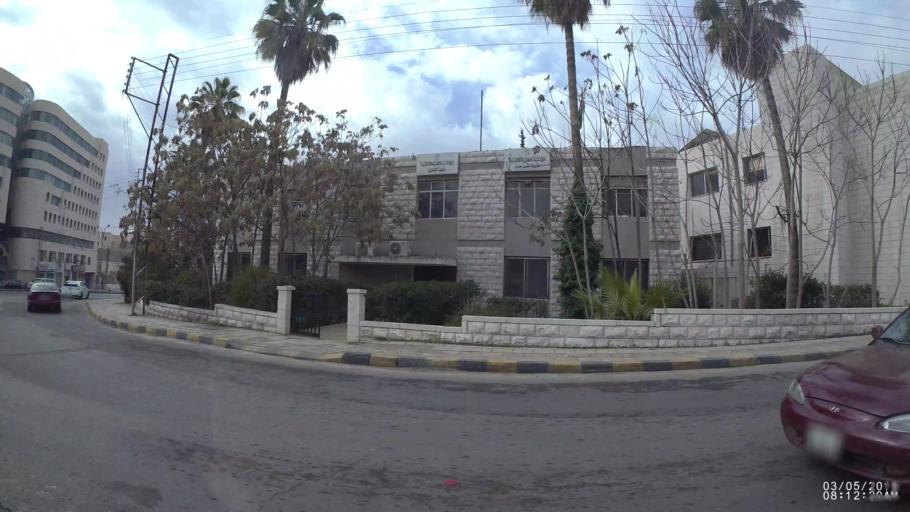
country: JO
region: Amman
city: Amman
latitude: 31.9689
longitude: 35.9084
